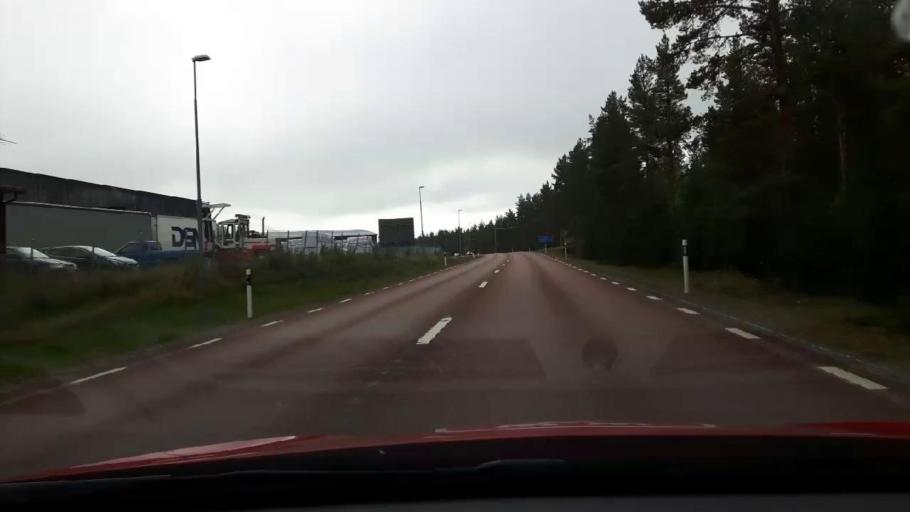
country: SE
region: Gaevleborg
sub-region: Ljusdals Kommun
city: Farila
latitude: 61.8065
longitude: 15.7778
